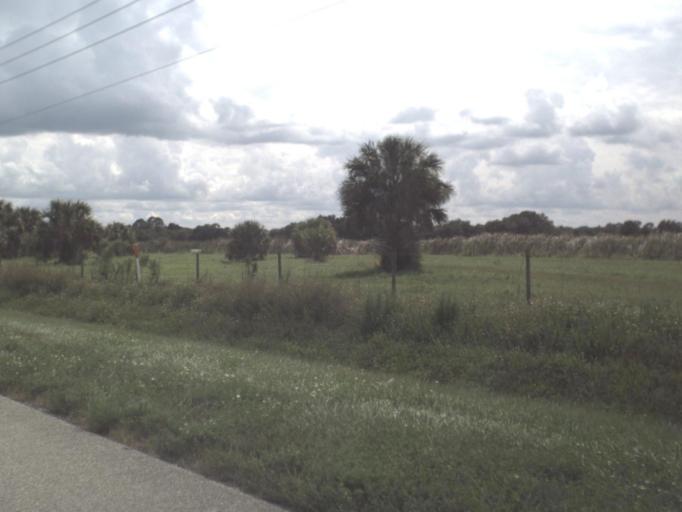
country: US
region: Florida
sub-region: DeSoto County
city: Nocatee
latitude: 27.0593
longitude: -81.7888
